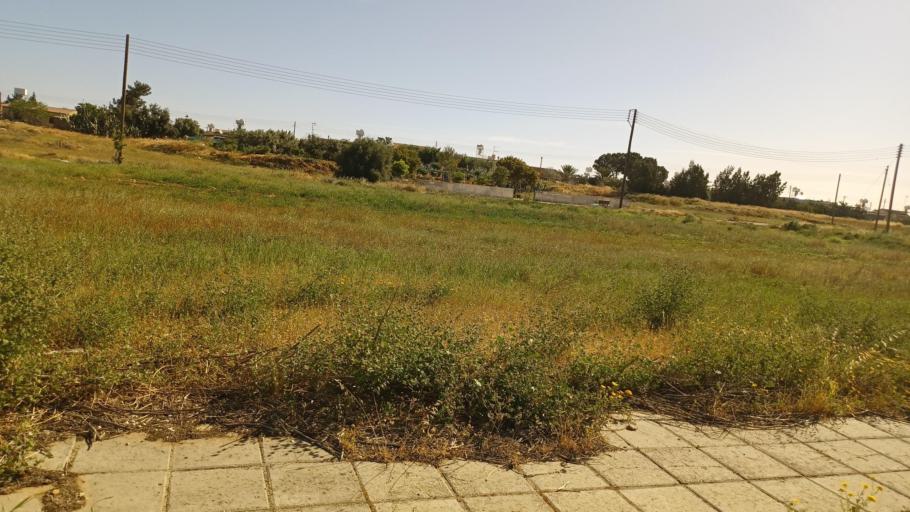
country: CY
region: Lefkosia
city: Kokkinotrimithia
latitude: 35.1534
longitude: 33.1857
